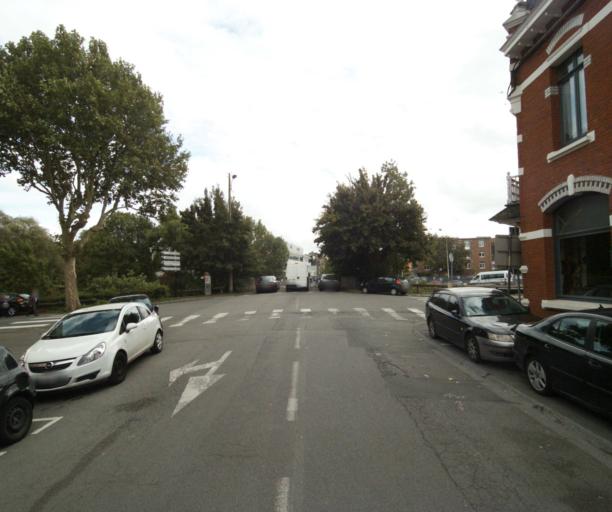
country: FR
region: Nord-Pas-de-Calais
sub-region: Departement du Nord
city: Lambersart
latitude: 50.6360
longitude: 3.0289
